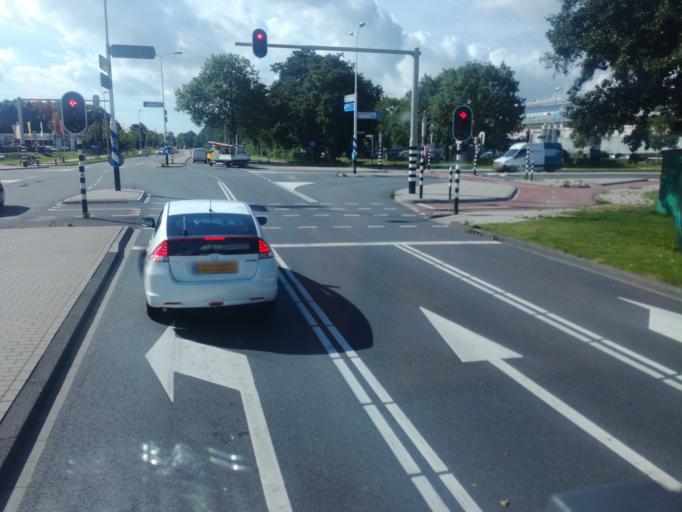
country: NL
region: North Holland
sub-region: Gemeente Hoorn
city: Hoorn
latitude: 52.6681
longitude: 5.0618
